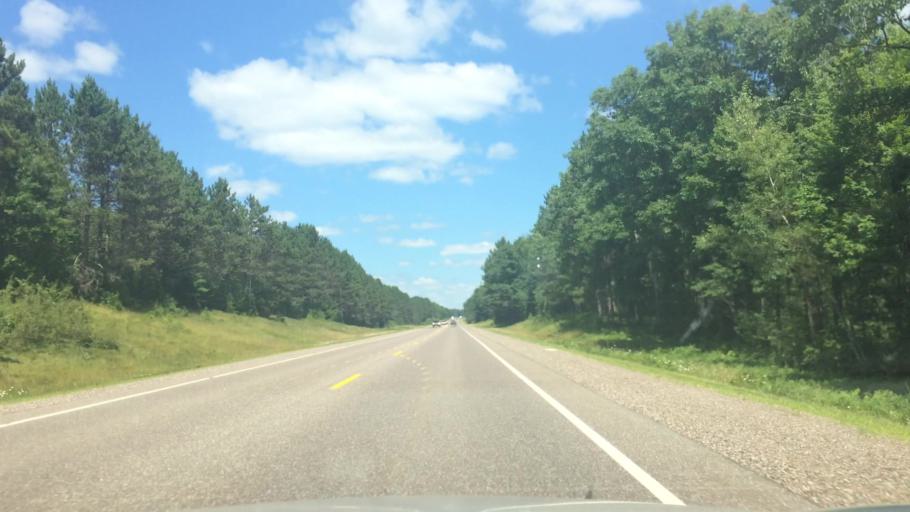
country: US
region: Wisconsin
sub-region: Vilas County
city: Lac du Flambeau
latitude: 45.9610
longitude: -89.7003
